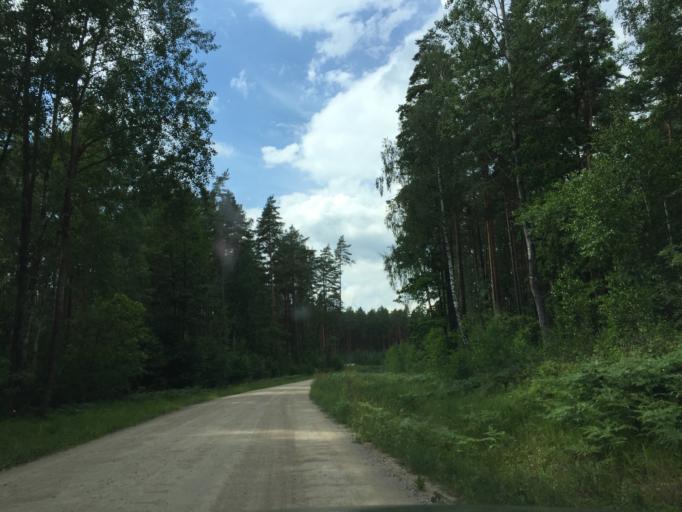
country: LV
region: Jelgava
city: Jelgava
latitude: 56.6263
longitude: 23.6549
